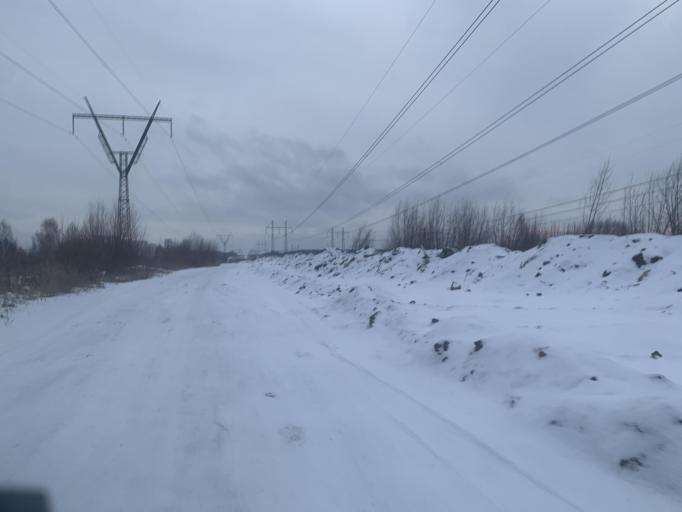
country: RU
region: Chelyabinsk
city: Roshchino
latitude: 55.1886
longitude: 61.2583
